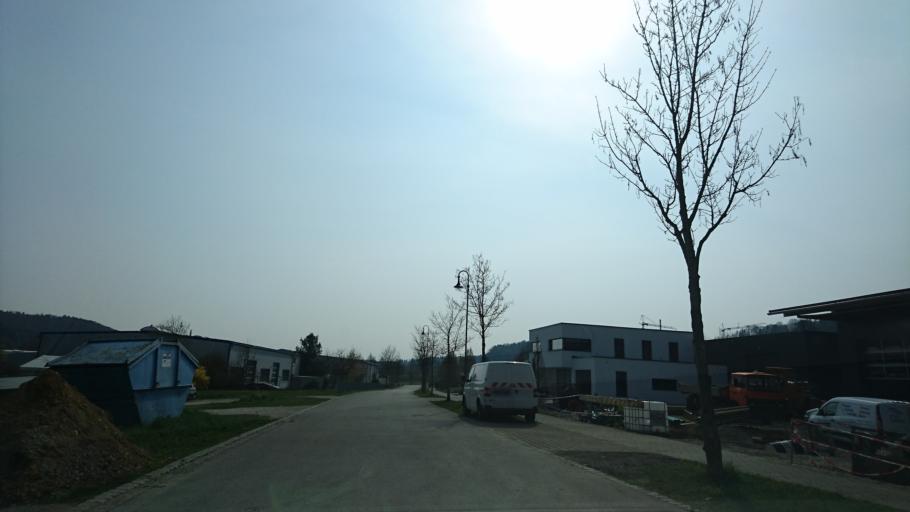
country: DE
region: Bavaria
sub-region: Swabia
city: Zusmarshausen
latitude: 48.3963
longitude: 10.6056
